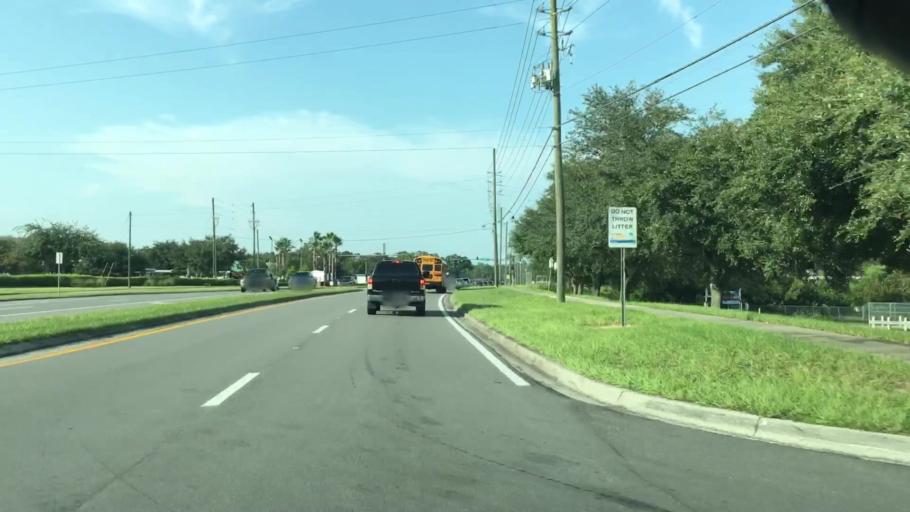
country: US
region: Florida
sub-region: Pasco County
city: Land O' Lakes
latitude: 28.1877
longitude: -82.4376
